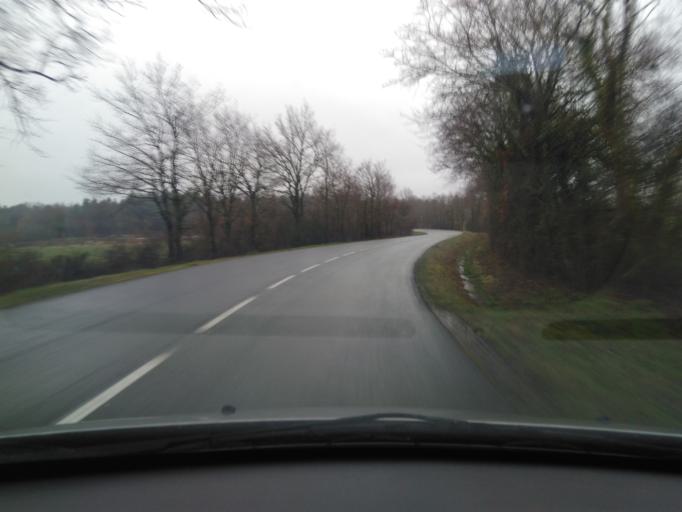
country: FR
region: Pays de la Loire
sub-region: Departement de la Vendee
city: La Chaize-le-Vicomte
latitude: 46.6907
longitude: -1.3042
